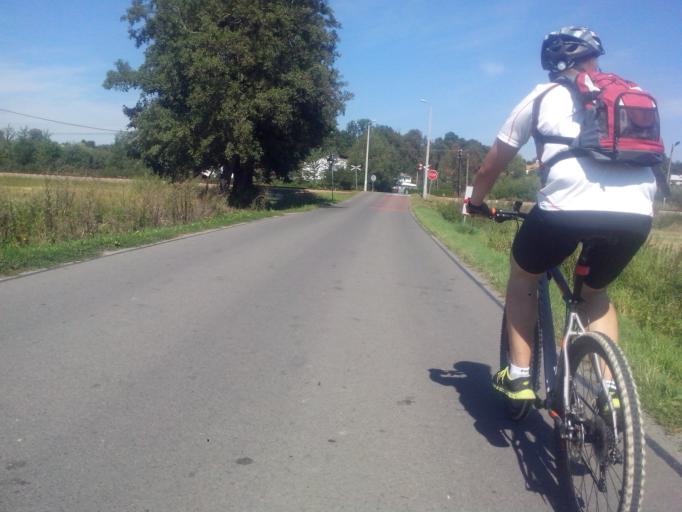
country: PL
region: Subcarpathian Voivodeship
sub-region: Powiat strzyzowski
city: Wisniowa
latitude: 49.8638
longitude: 21.6472
